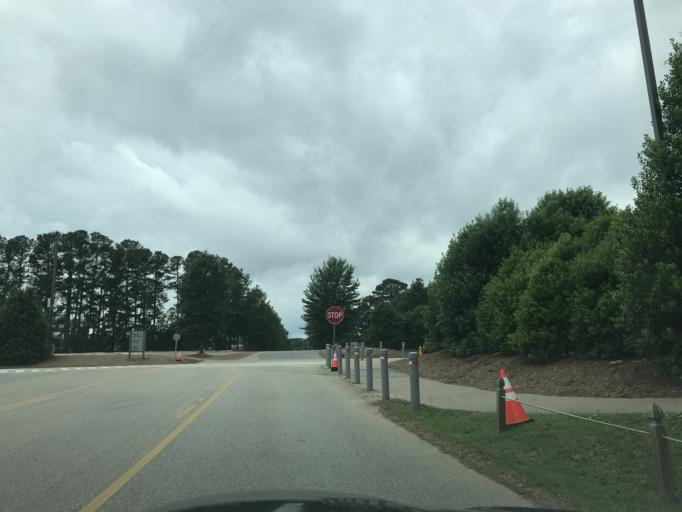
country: US
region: North Carolina
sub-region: Wake County
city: West Raleigh
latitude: 35.8024
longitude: -78.7165
